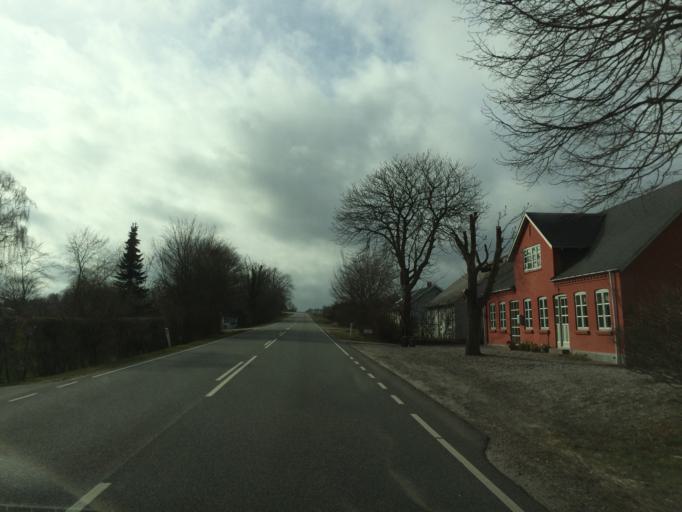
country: DK
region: Central Jutland
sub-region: Favrskov Kommune
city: Ulstrup
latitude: 56.4945
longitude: 9.8436
